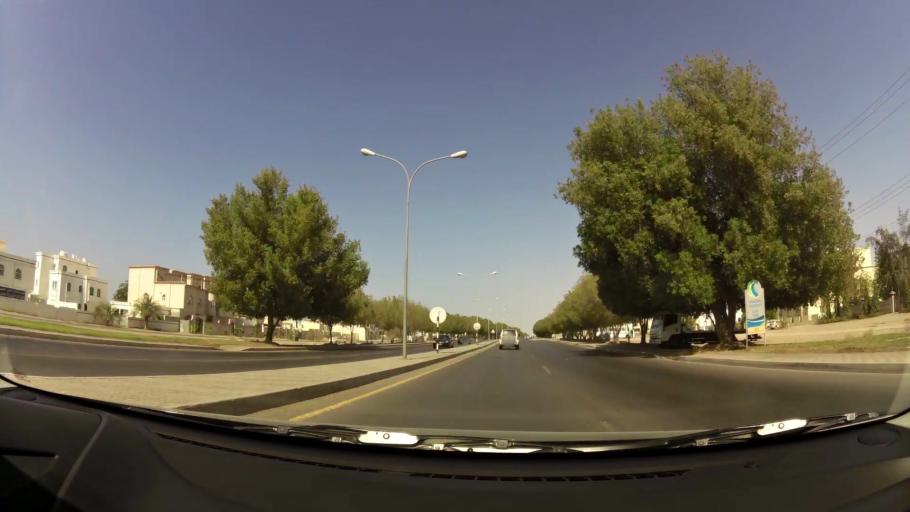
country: OM
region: Muhafazat Masqat
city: As Sib al Jadidah
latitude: 23.6142
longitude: 58.2202
